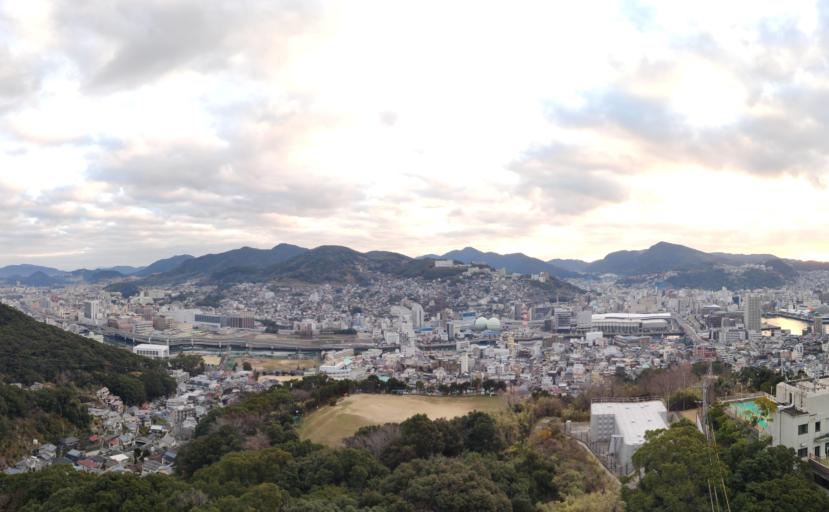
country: JP
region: Nagasaki
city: Nagasaki-shi
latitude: 32.7538
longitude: 129.8558
